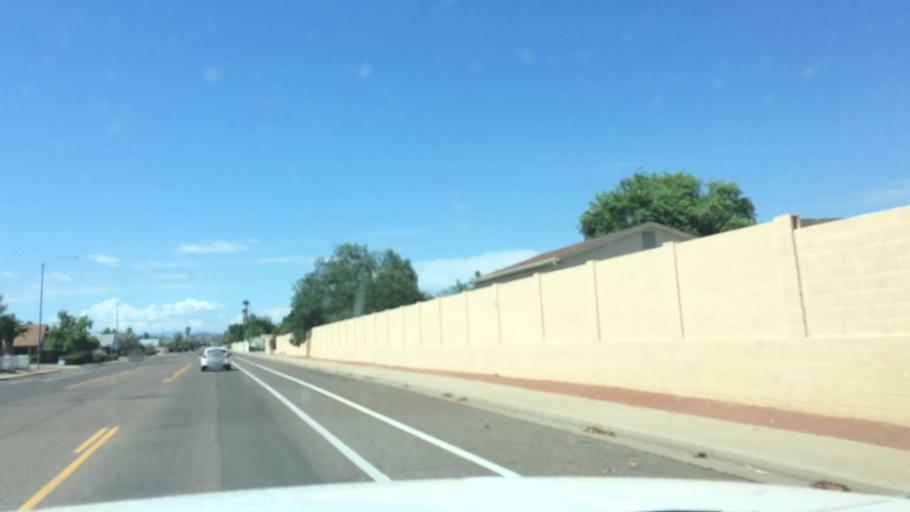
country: US
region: Arizona
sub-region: Maricopa County
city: Sun City
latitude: 33.6436
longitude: -112.2463
